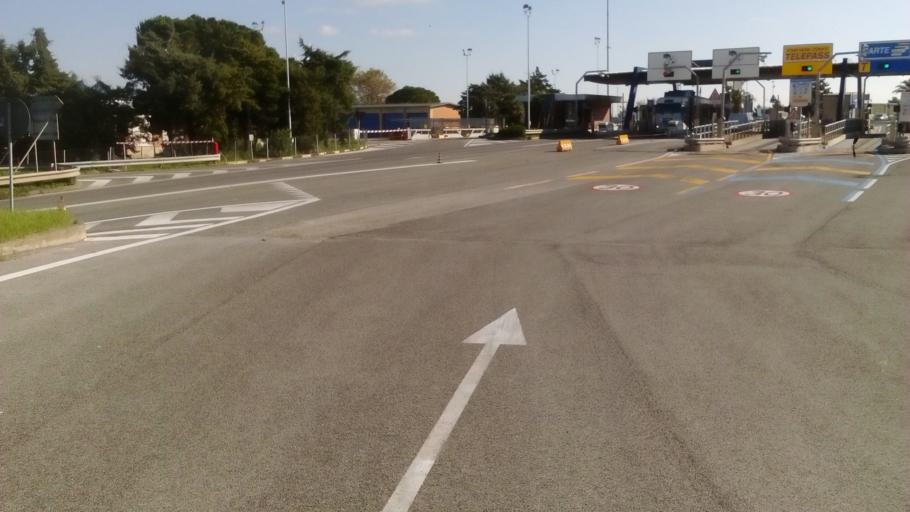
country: IT
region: Apulia
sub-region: Provincia di Foggia
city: Candela
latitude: 41.1514
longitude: 15.5255
